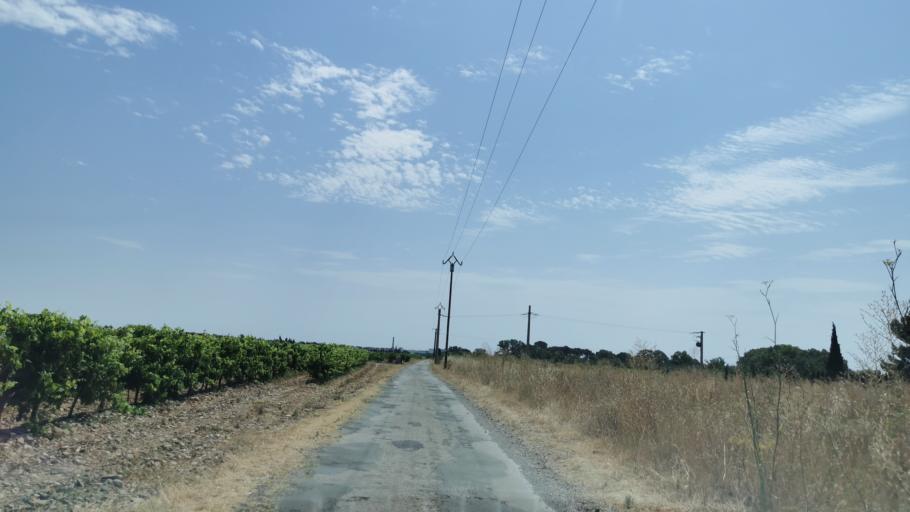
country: FR
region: Languedoc-Roussillon
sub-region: Departement de l'Aude
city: Argeliers
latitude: 43.2890
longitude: 2.8934
